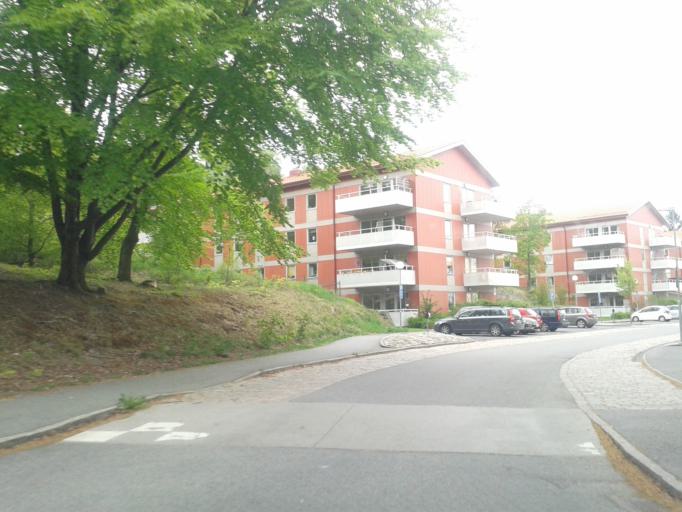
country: SE
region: Vaestra Goetaland
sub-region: Kungalvs Kommun
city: Kungalv
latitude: 57.8686
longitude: 11.9920
